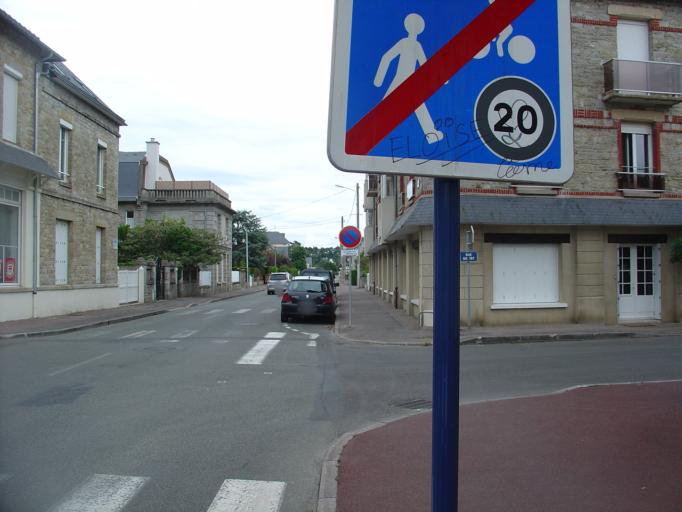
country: FR
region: Brittany
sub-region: Departement des Cotes-d'Armor
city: Saint-Cast-le-Guildo
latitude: 48.6311
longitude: -2.2551
